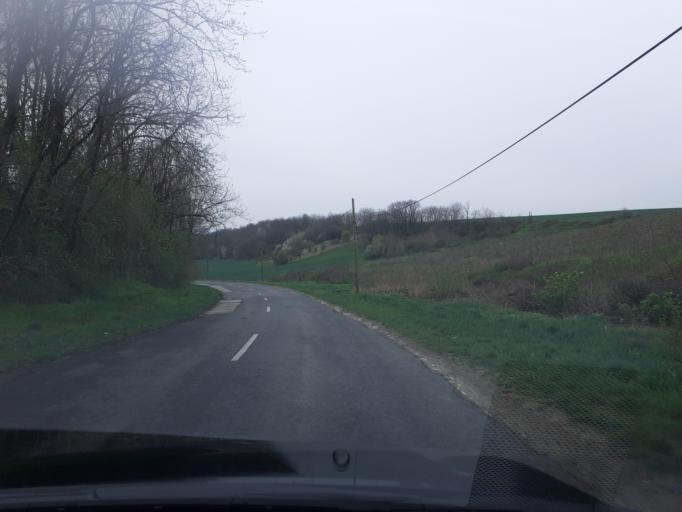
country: HU
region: Tolna
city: Hogyesz
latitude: 46.4311
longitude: 18.4500
